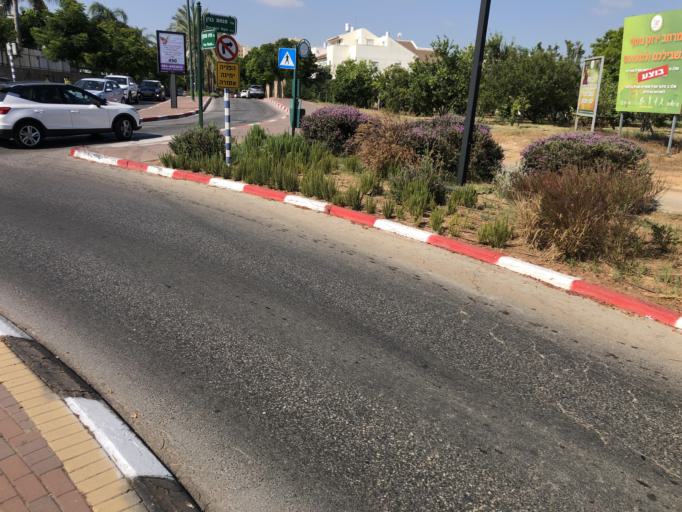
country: IL
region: Central District
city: Yehud
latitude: 32.0381
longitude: 34.8831
